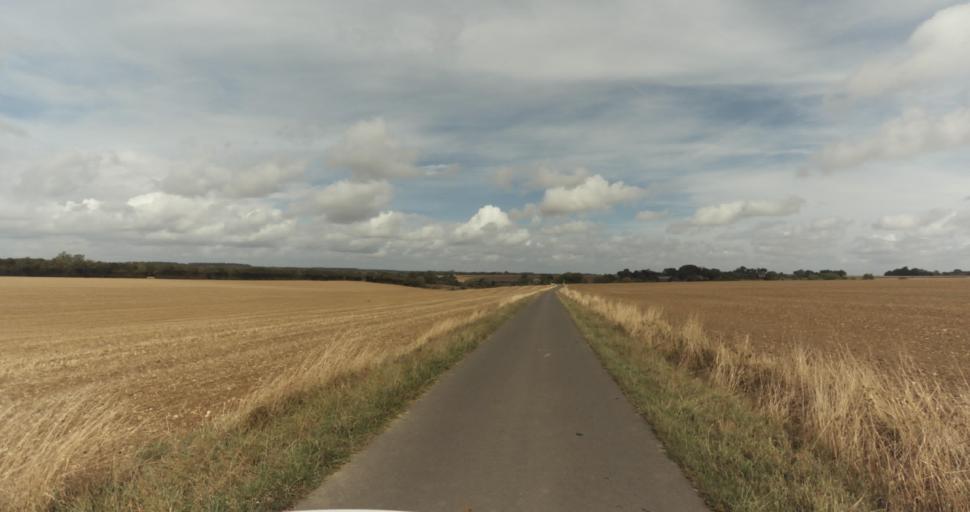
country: FR
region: Lower Normandy
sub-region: Departement de l'Orne
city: Gace
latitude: 48.8038
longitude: 0.3756
